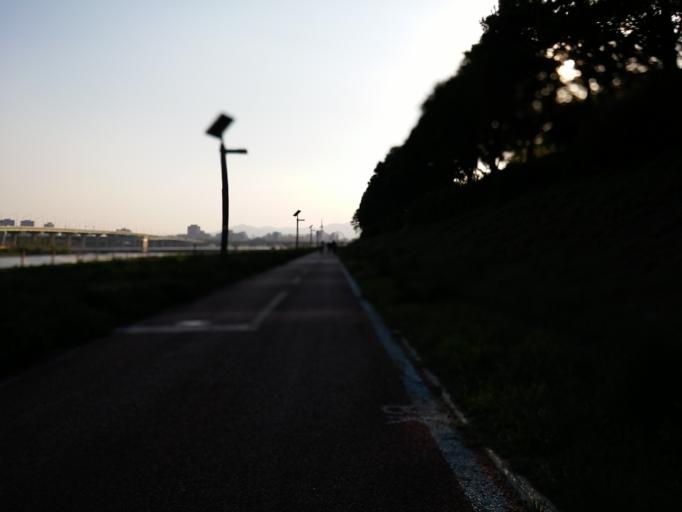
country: KR
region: Daejeon
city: Daejeon
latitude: 36.3764
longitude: 127.4032
